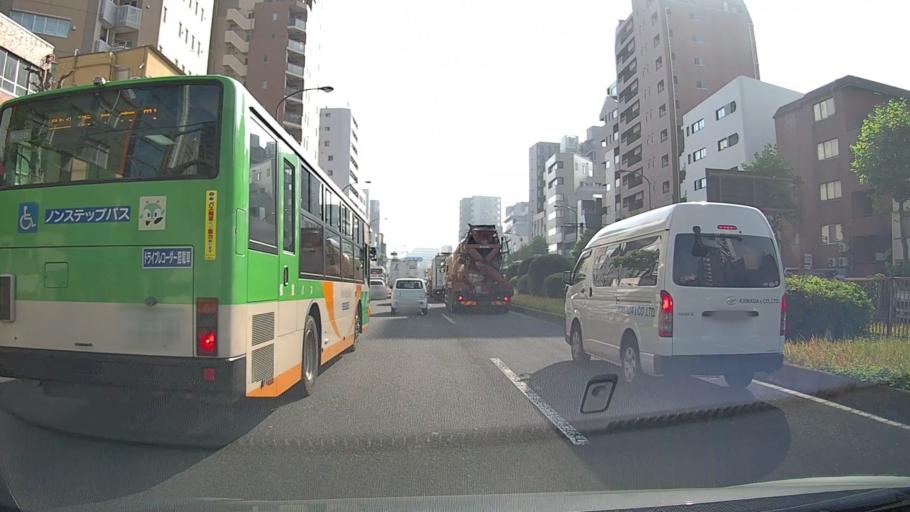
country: JP
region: Tokyo
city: Tokyo
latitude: 35.7305
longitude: 139.7420
